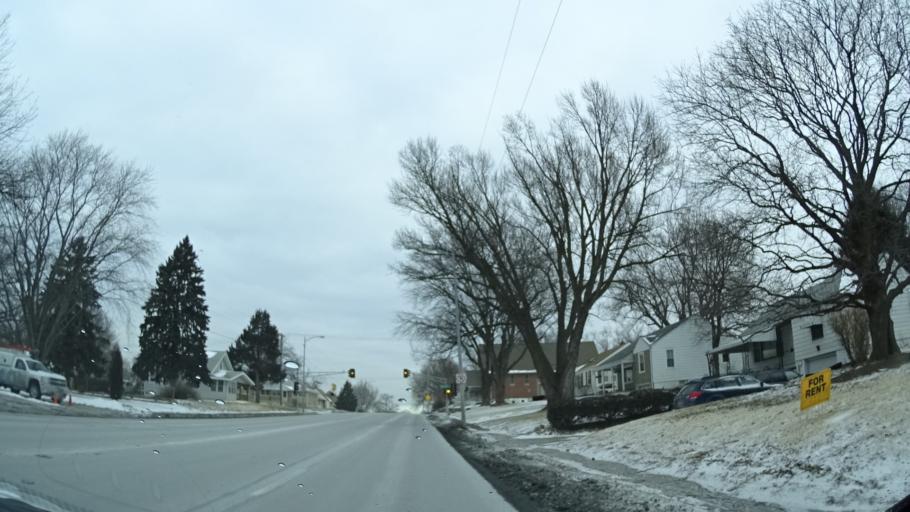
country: US
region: Nebraska
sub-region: Douglas County
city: Omaha
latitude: 41.2334
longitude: -95.9758
